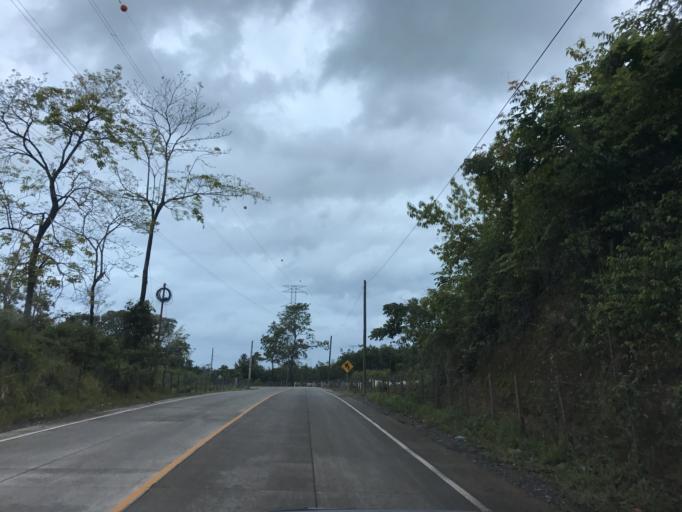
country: GT
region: Izabal
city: Morales
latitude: 15.6295
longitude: -89.0531
